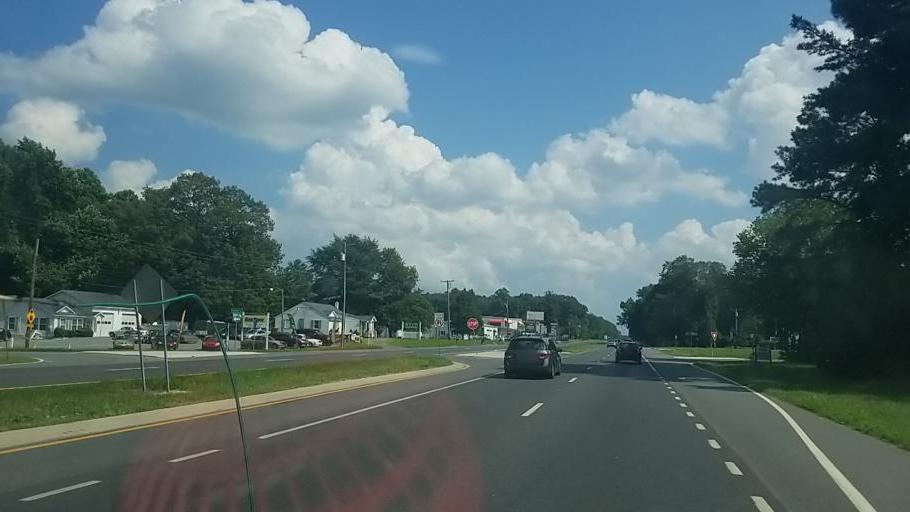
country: US
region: Delaware
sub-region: Sussex County
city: Millsboro
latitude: 38.5639
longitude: -75.2765
